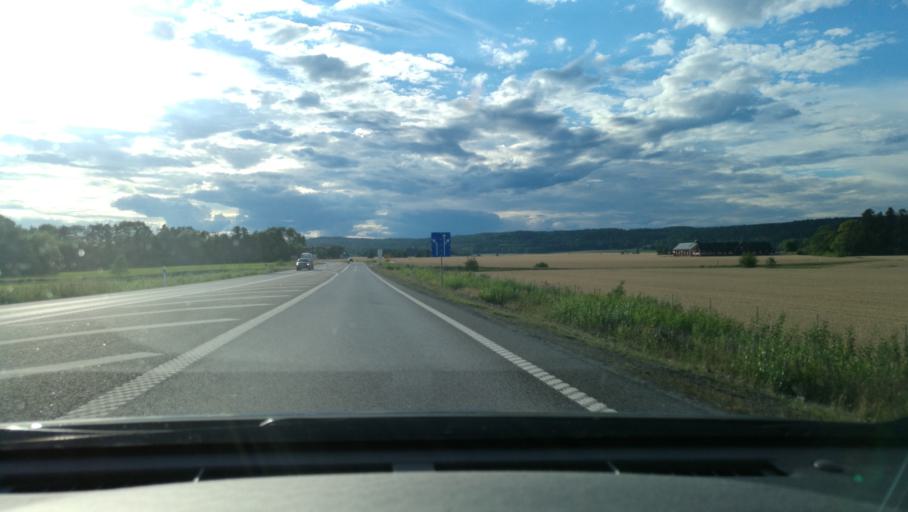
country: SE
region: OEstergoetland
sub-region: Norrkopings Kommun
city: Norrkoping
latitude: 58.6297
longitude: 16.1461
